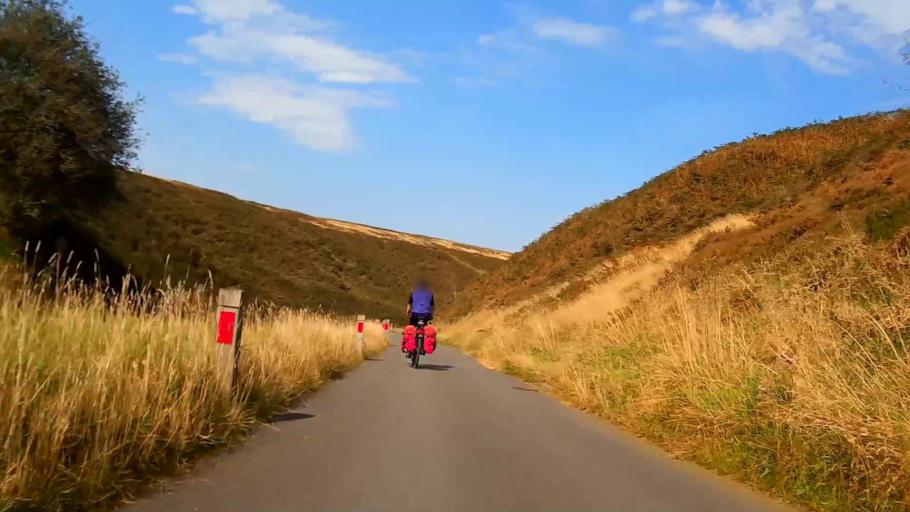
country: GB
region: England
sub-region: Derbyshire
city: Buxton
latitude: 53.2426
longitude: -1.9760
